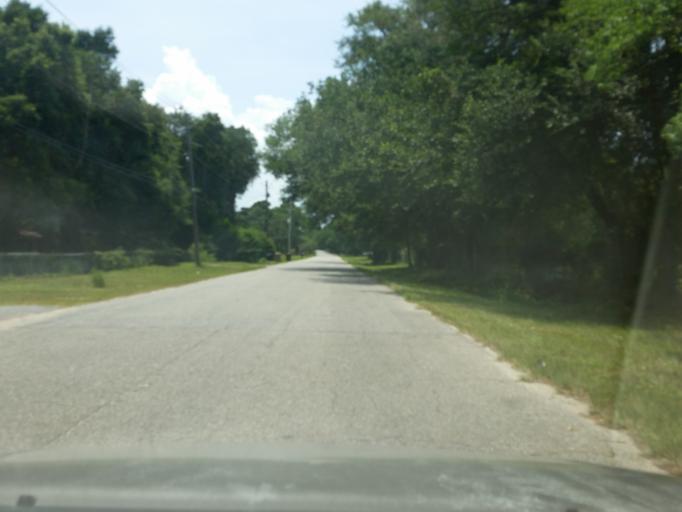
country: US
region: Florida
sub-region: Escambia County
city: Ferry Pass
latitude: 30.5011
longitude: -87.2082
